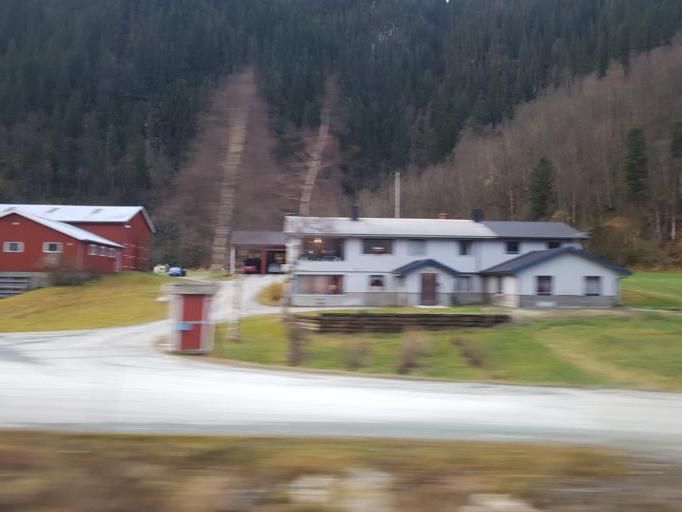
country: NO
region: Sor-Trondelag
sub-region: Midtre Gauldal
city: Storen
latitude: 63.0775
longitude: 10.2609
